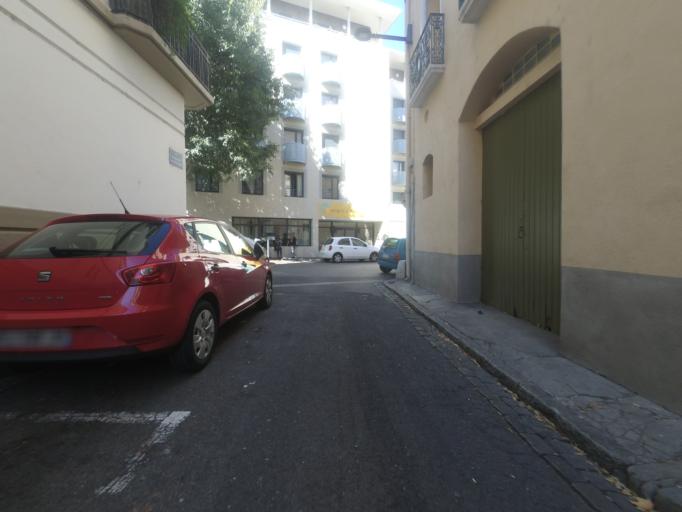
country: FR
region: Languedoc-Roussillon
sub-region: Departement des Pyrenees-Orientales
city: Perpignan
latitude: 42.7021
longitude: 2.8921
